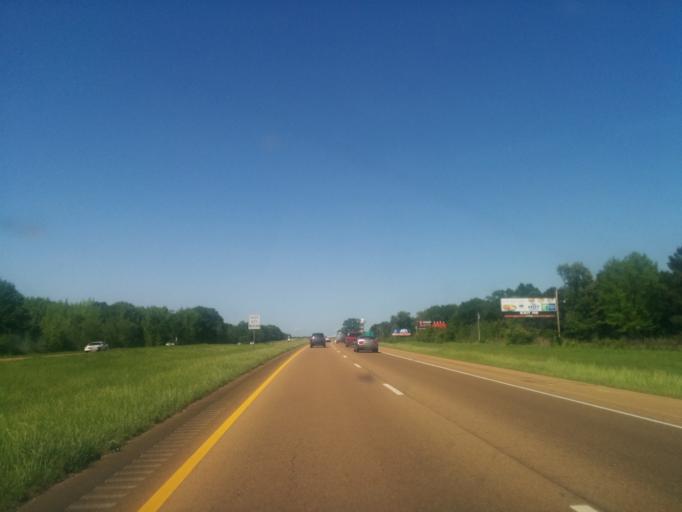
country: US
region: Mississippi
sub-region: Madison County
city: Canton
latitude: 32.5507
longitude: -90.0884
